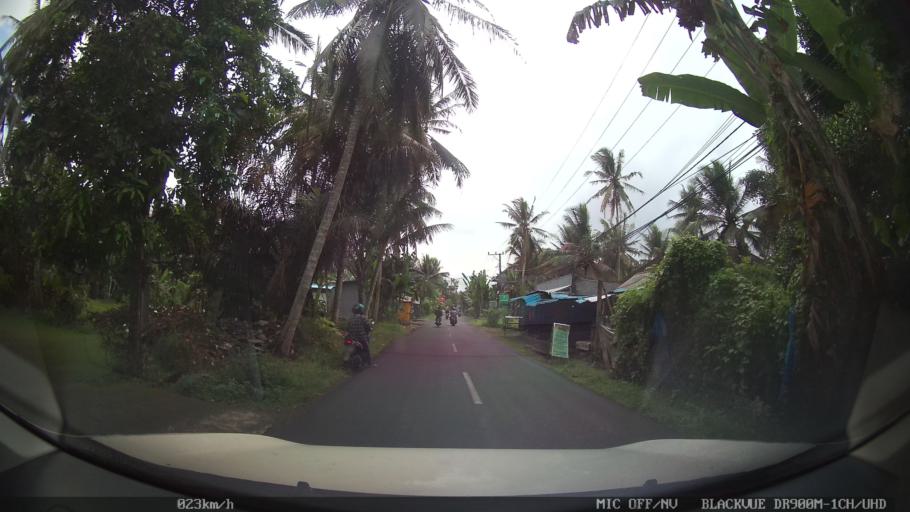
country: ID
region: Bali
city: Banjar Parekan
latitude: -8.5699
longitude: 115.2097
